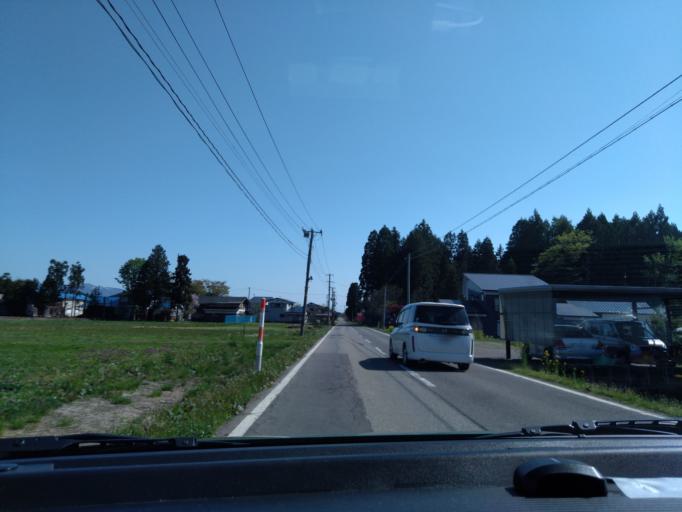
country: JP
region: Akita
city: Kakunodatemachi
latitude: 39.5488
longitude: 140.5859
